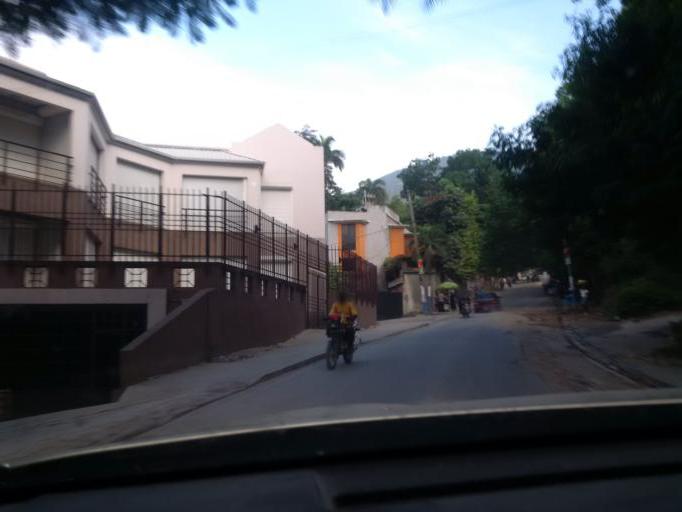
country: HT
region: Ouest
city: Port-au-Prince
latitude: 18.5308
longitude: -72.3223
